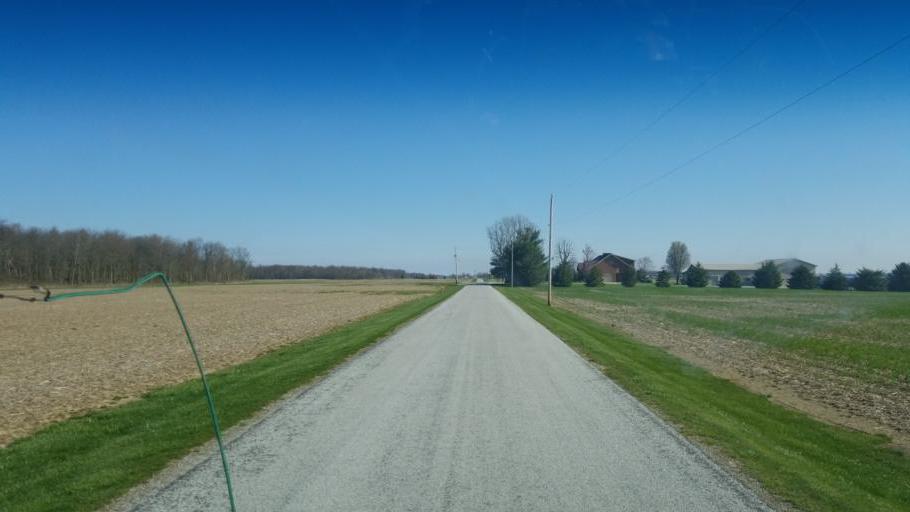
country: US
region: Ohio
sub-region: Hardin County
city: Kenton
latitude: 40.6670
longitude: -83.5622
